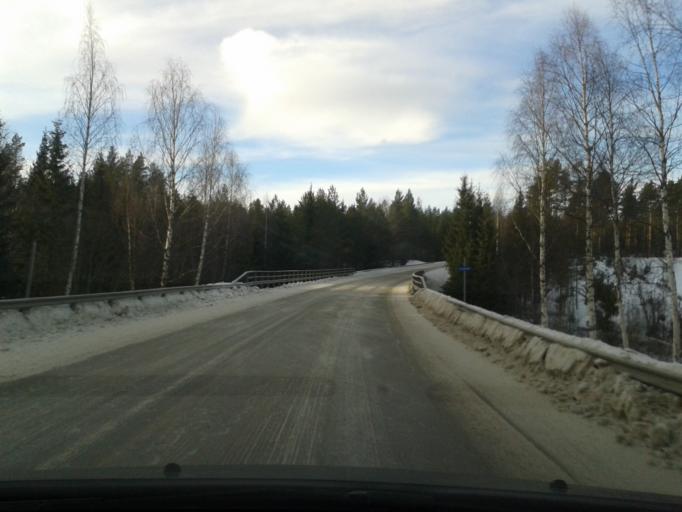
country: SE
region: Vaesternorrland
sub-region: OErnskoeldsviks Kommun
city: Bredbyn
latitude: 63.5305
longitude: 17.9730
